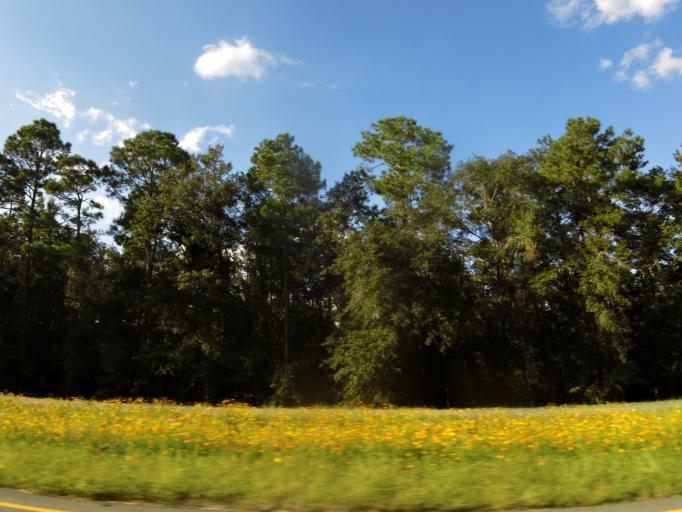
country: US
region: Georgia
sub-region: Lowndes County
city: Remerton
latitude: 30.7971
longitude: -83.4038
